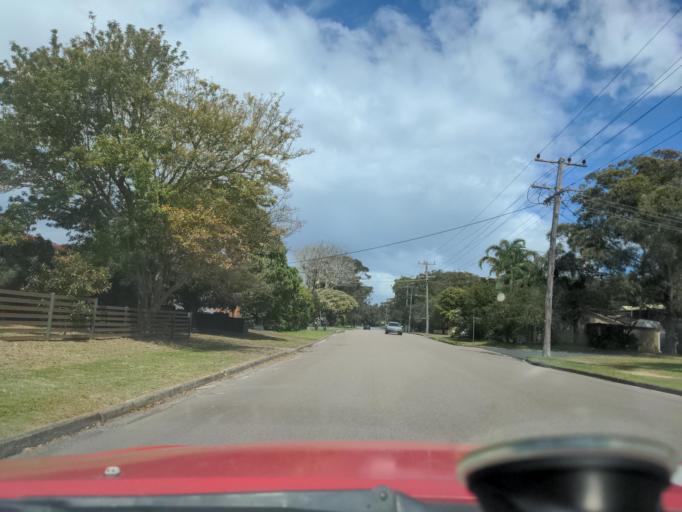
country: AU
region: New South Wales
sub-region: Great Lakes
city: Hawks Nest
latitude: -32.6735
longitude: 152.1772
